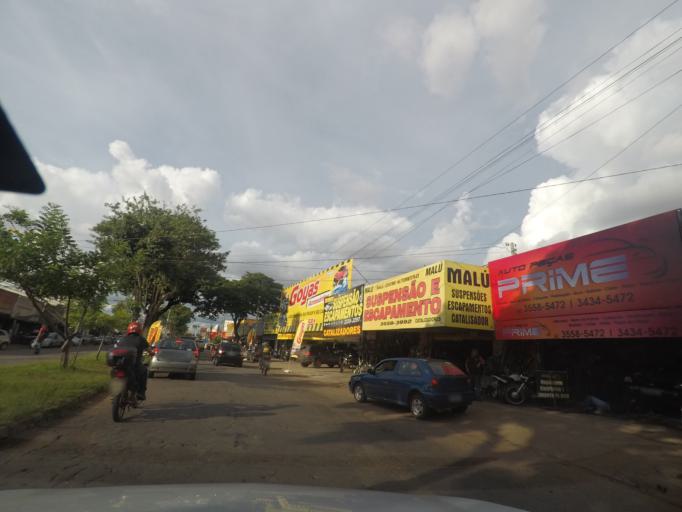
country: BR
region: Goias
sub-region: Goiania
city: Goiania
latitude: -16.6914
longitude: -49.3160
